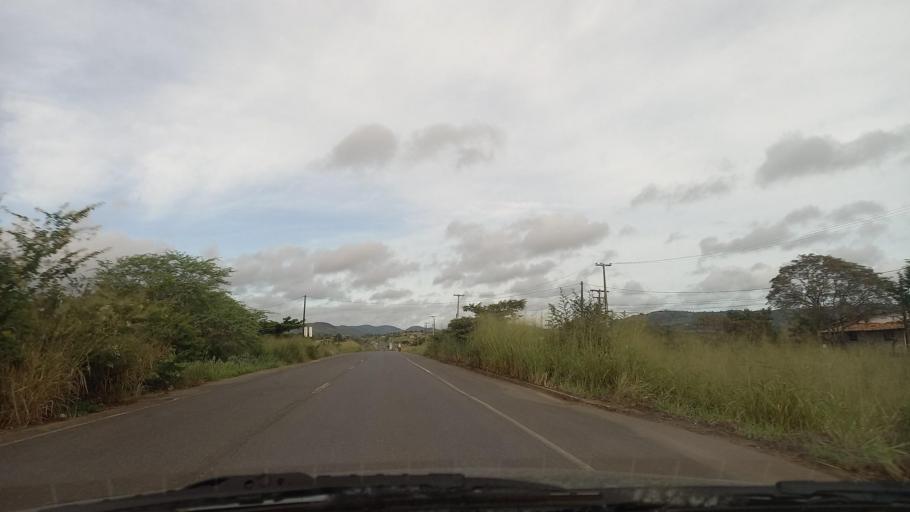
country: BR
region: Pernambuco
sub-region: Pombos
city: Pombos
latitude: -8.1270
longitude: -35.3512
